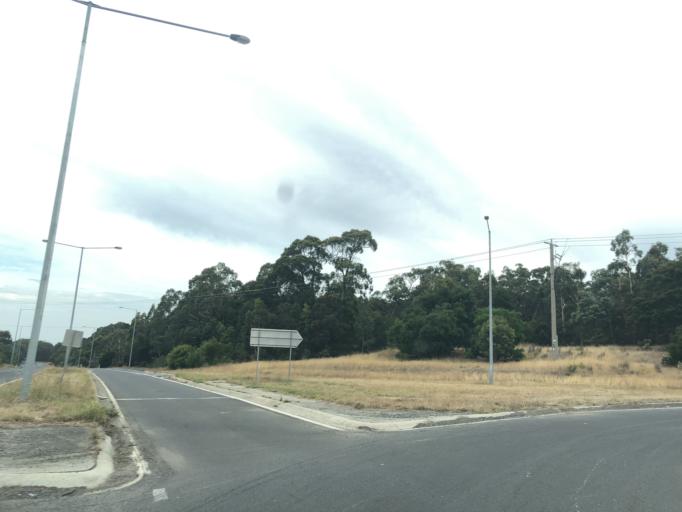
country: AU
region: Victoria
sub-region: Hume
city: Sunbury
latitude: -37.4153
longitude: 144.5460
